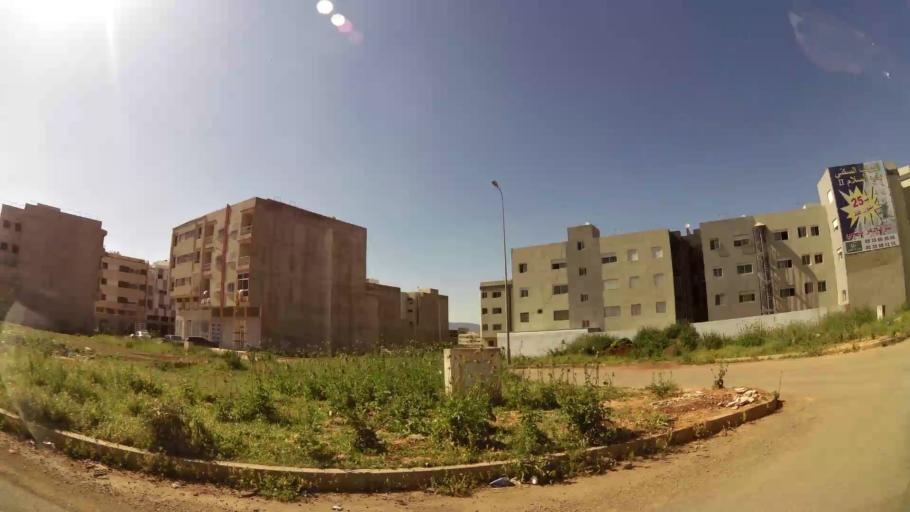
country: MA
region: Fes-Boulemane
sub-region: Fes
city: Fes
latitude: 33.9950
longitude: -5.0047
